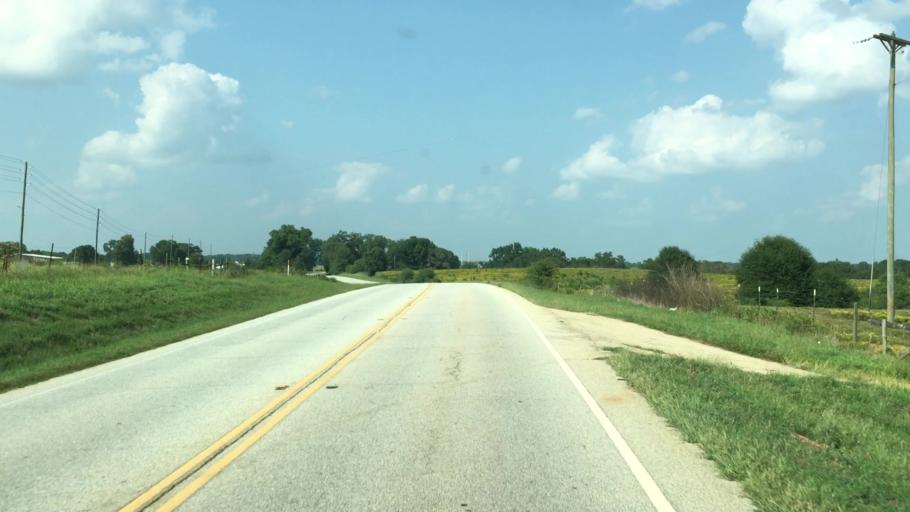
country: US
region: Georgia
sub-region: Newton County
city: Covington
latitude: 33.4825
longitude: -83.7442
